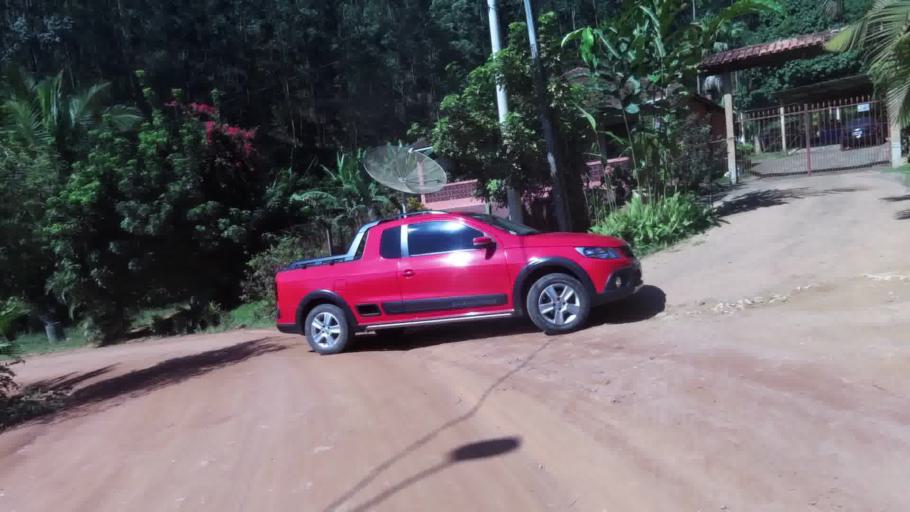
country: BR
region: Espirito Santo
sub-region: Alfredo Chaves
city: Alfredo Chaves
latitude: -20.6465
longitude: -40.7940
